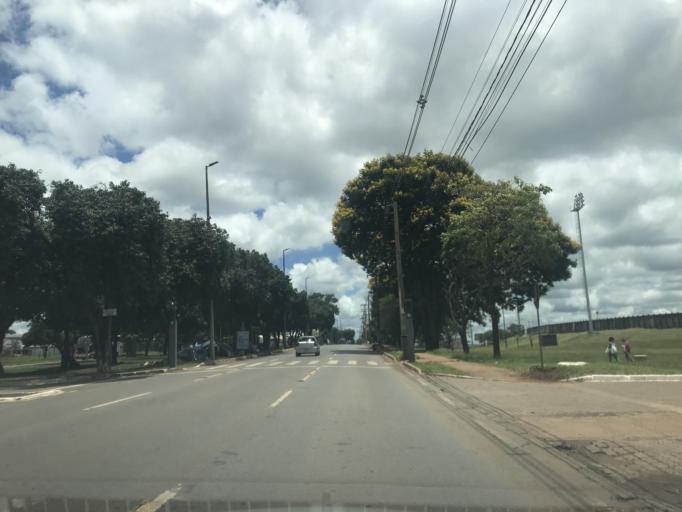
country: BR
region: Federal District
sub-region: Brasilia
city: Brasilia
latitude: -15.6508
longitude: -47.7846
